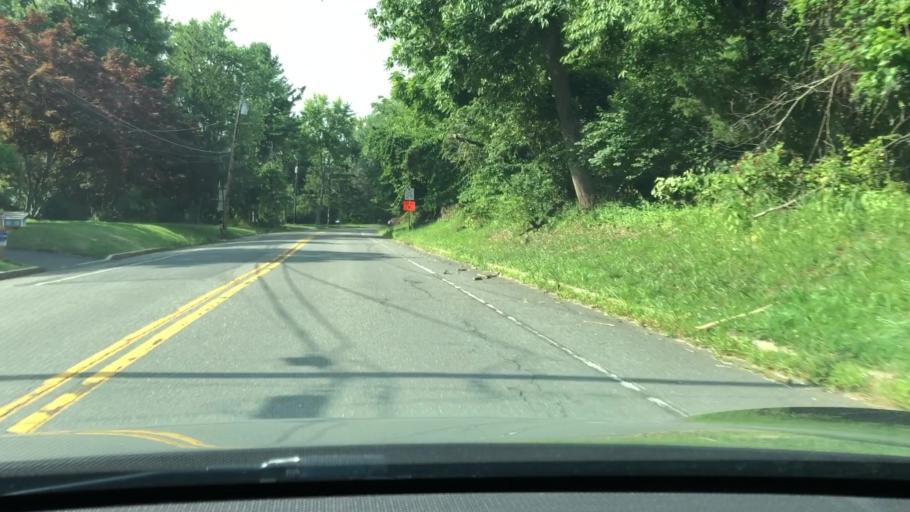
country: US
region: New Jersey
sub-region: Mercer County
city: Pennington
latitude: 40.3265
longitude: -74.8164
